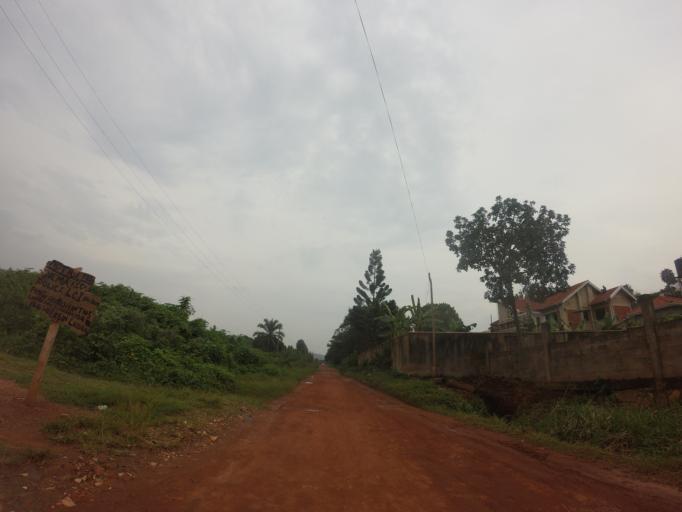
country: UG
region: Central Region
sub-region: Wakiso District
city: Kireka
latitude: 0.3541
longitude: 32.6219
